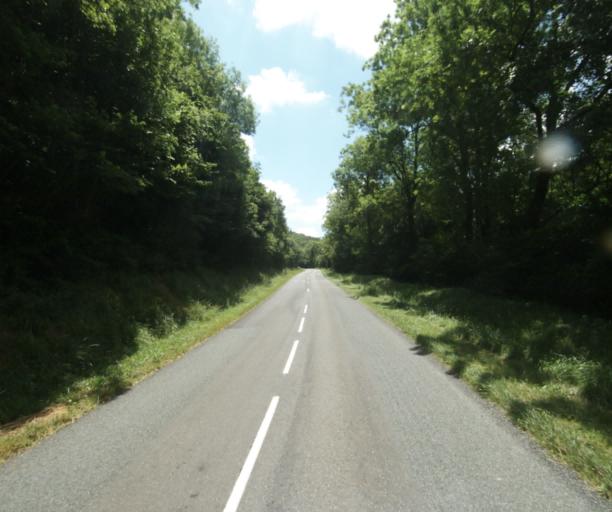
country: FR
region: Midi-Pyrenees
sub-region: Departement du Tarn
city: Soreze
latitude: 43.4241
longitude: 2.0572
